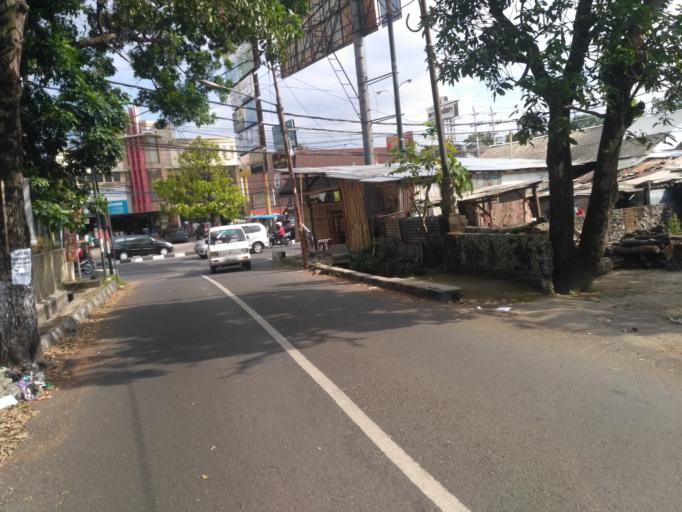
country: ID
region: Daerah Istimewa Yogyakarta
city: Depok
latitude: -7.7830
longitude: 110.4052
